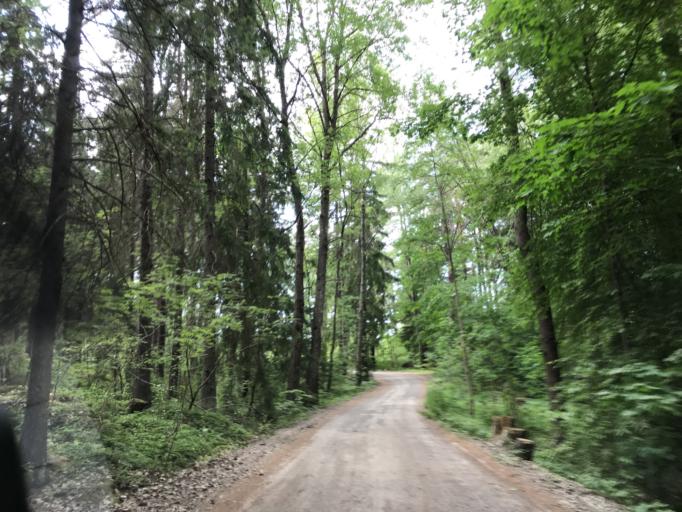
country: SE
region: Stockholm
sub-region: Solna Kommun
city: Rasunda
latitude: 59.4047
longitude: 17.9876
